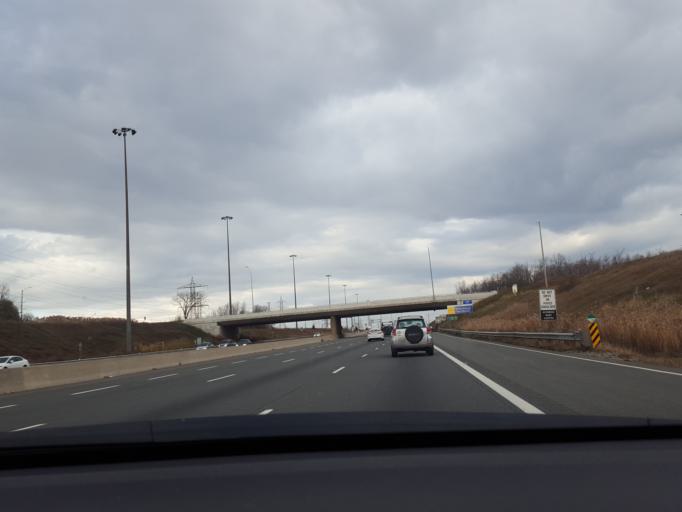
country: CA
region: Ontario
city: Mississauga
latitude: 43.5700
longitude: -79.6754
